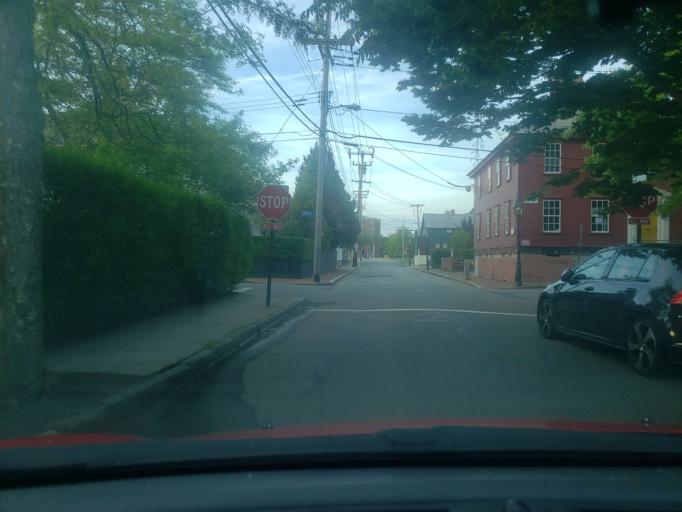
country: US
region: Rhode Island
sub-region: Newport County
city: Newport
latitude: 41.4923
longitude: -71.3195
